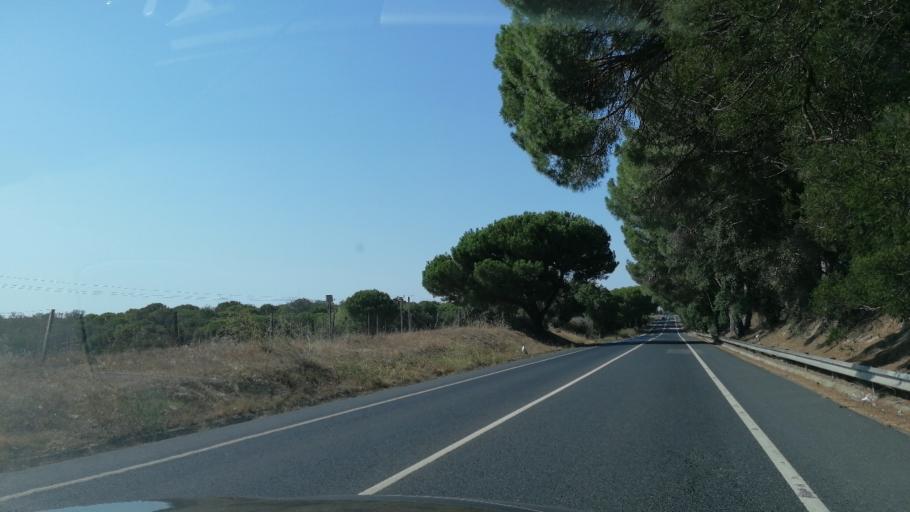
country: PT
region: Evora
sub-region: Vendas Novas
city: Vendas Novas
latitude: 38.7045
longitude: -8.6129
